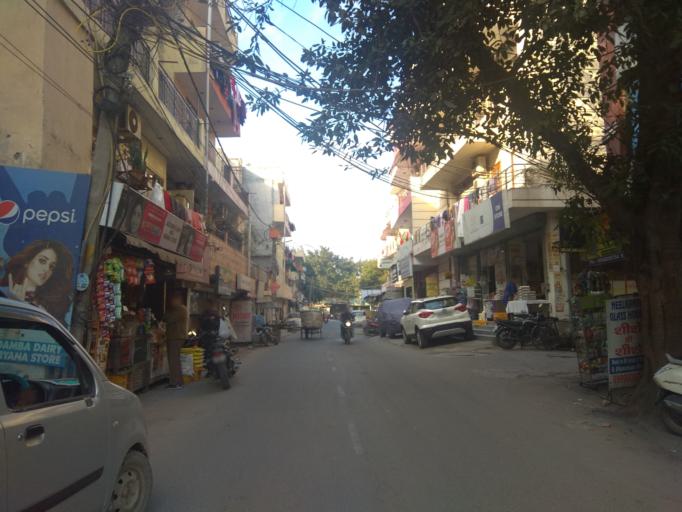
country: IN
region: NCT
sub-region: West Delhi
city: Nangloi Jat
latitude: 28.6368
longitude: 77.0678
